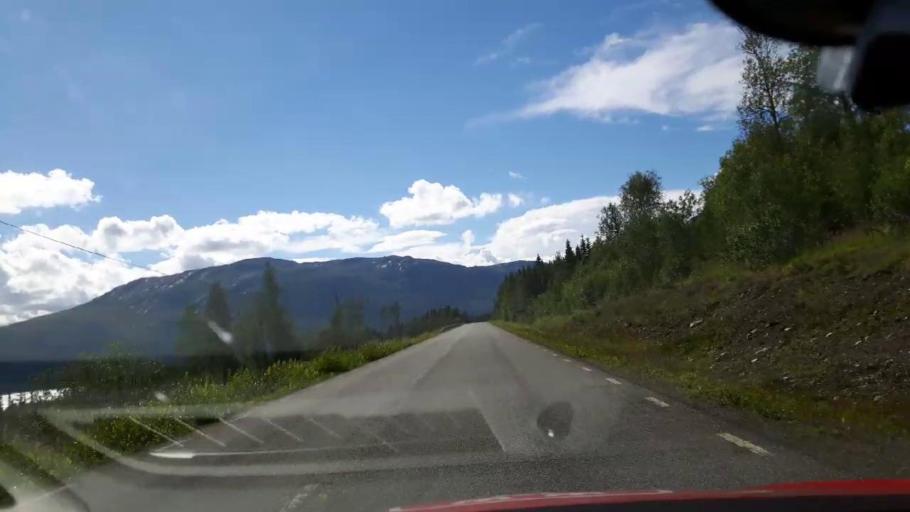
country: SE
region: Jaemtland
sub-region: Are Kommun
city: Are
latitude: 63.2175
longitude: 13.0844
